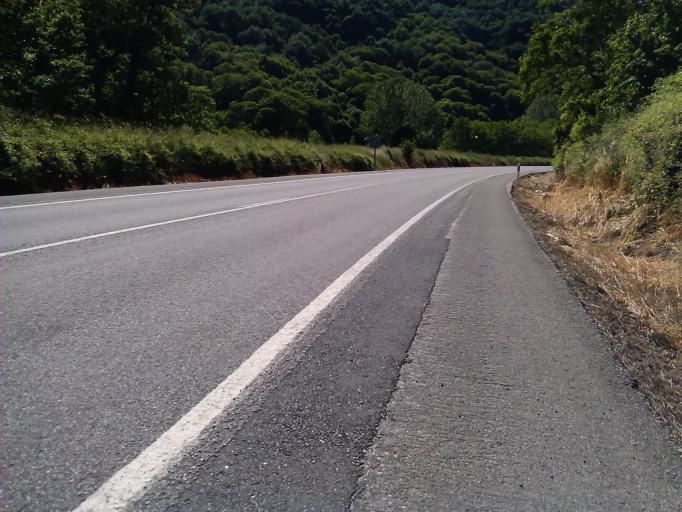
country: ES
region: Castille and Leon
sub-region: Provincia de Leon
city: Trabadelo
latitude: 42.6490
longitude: -6.8855
